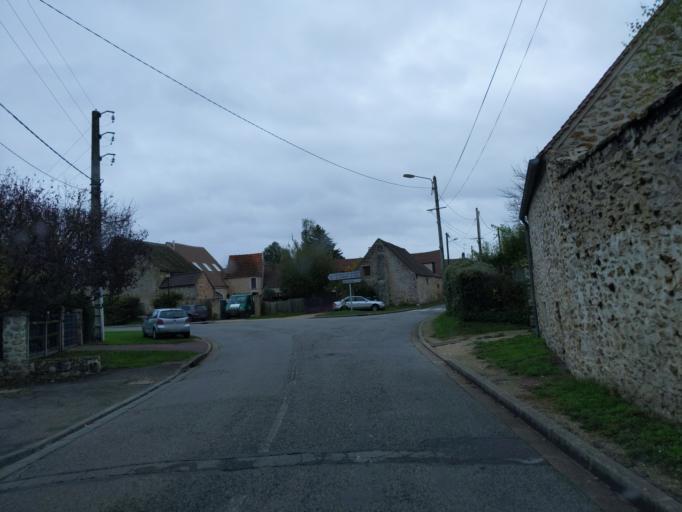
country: FR
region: Ile-de-France
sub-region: Departement des Yvelines
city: Bullion
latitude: 48.6233
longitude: 1.9905
